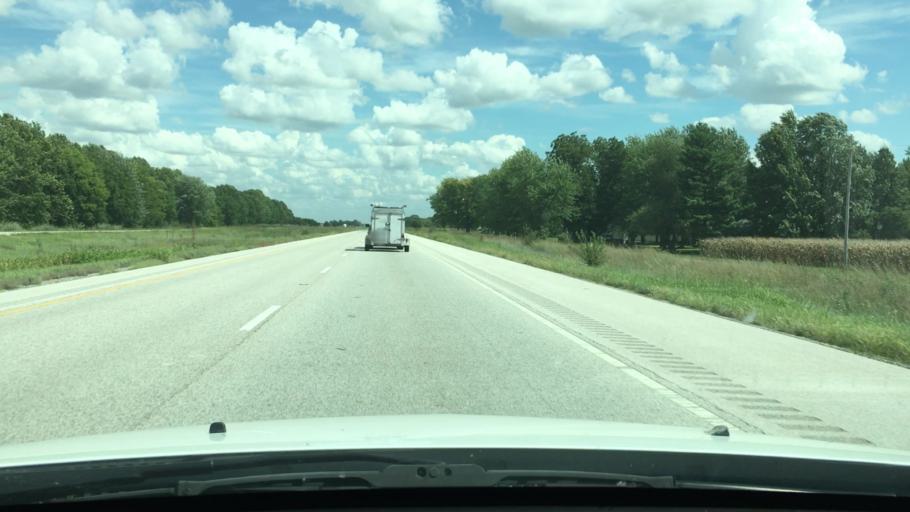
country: US
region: Illinois
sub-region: Morgan County
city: South Jacksonville
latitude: 39.6802
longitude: -90.3226
